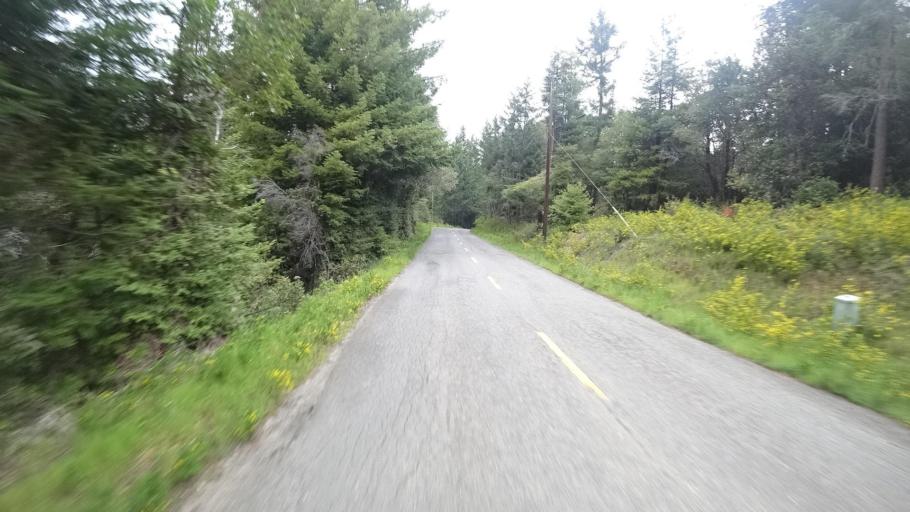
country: US
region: California
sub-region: Humboldt County
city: Redway
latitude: 40.2798
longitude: -123.7971
